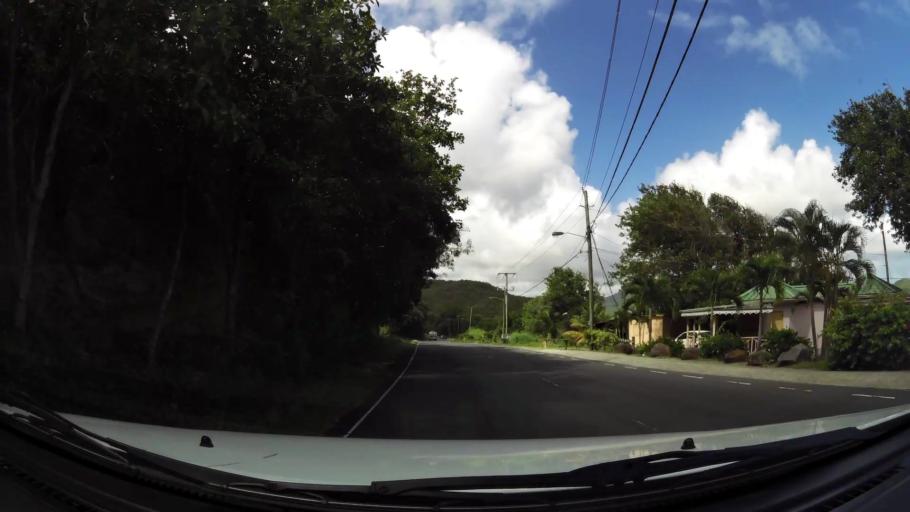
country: LC
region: Dennery Quarter
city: Dennery
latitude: 13.9184
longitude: -60.8935
